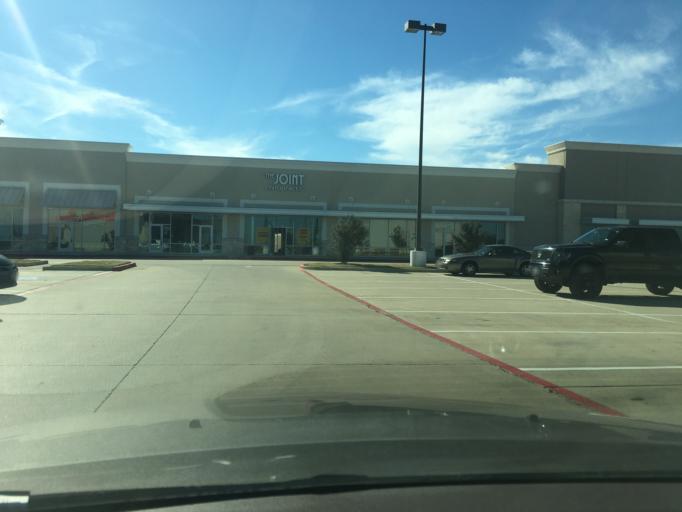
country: US
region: Texas
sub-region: Fort Bend County
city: Richmond
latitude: 29.5429
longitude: -95.7434
